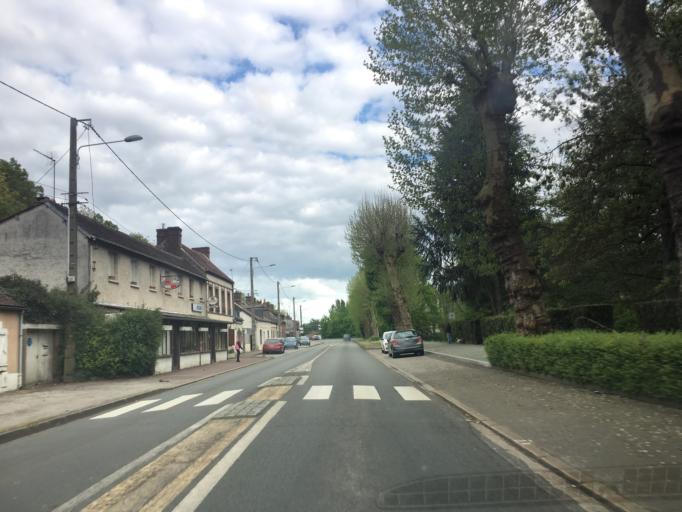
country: FR
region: Centre
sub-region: Departement d'Eure-et-Loir
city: Saint-Lubin-des-Joncherets
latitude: 48.7665
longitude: 1.2085
